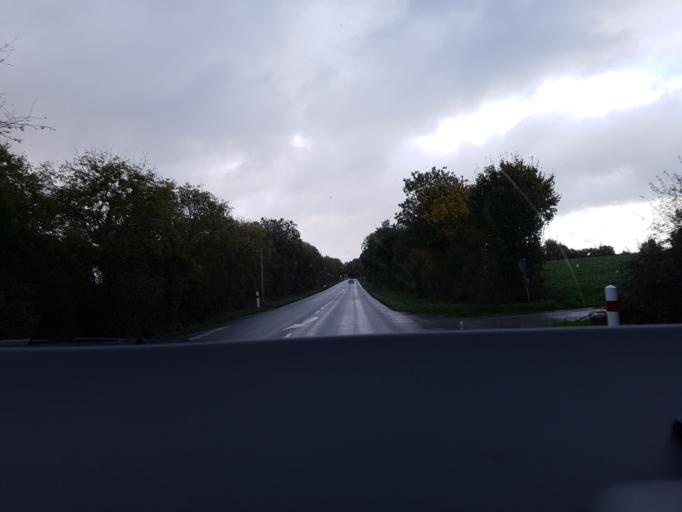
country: FR
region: Poitou-Charentes
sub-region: Departement des Deux-Sevres
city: Melle
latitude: 46.2046
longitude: -0.1552
